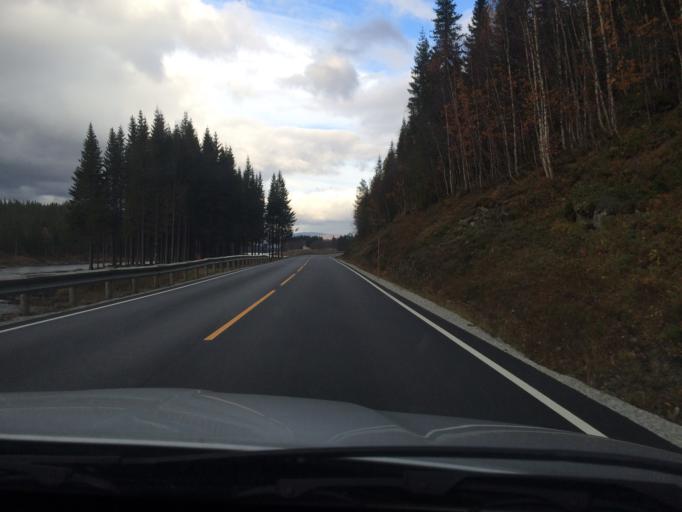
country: NO
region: Nord-Trondelag
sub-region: Namsskogan
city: Namsskogan
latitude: 64.7917
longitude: 12.9163
